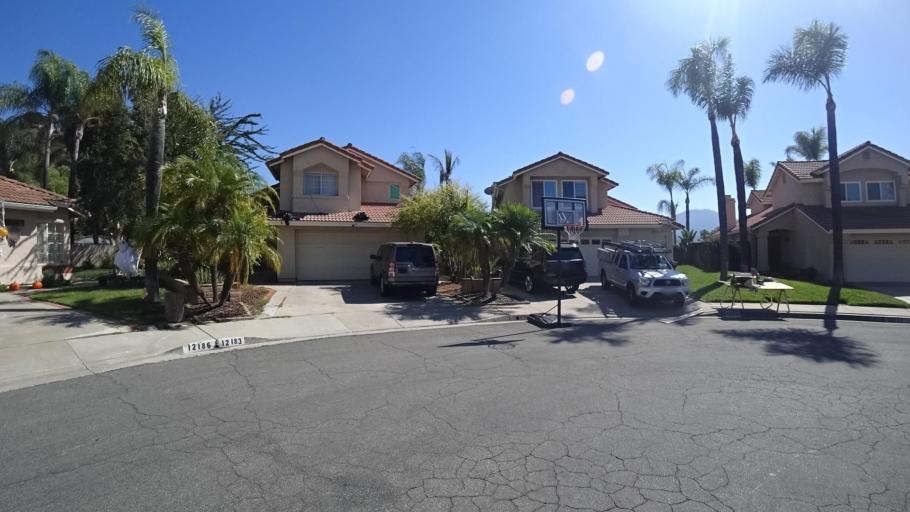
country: US
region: California
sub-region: San Diego County
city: Rancho San Diego
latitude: 32.7520
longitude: -116.9327
